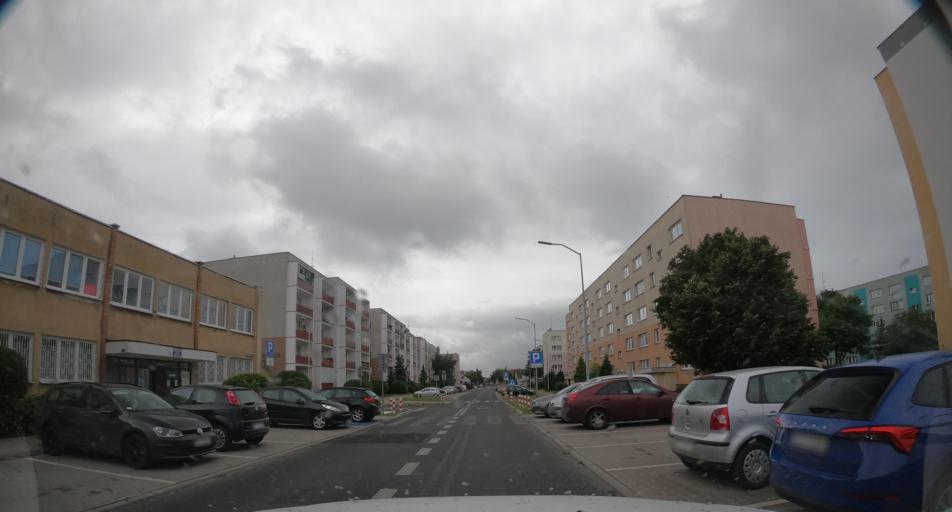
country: PL
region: West Pomeranian Voivodeship
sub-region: Powiat stargardzki
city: Stargard Szczecinski
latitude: 53.3466
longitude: 15.0075
